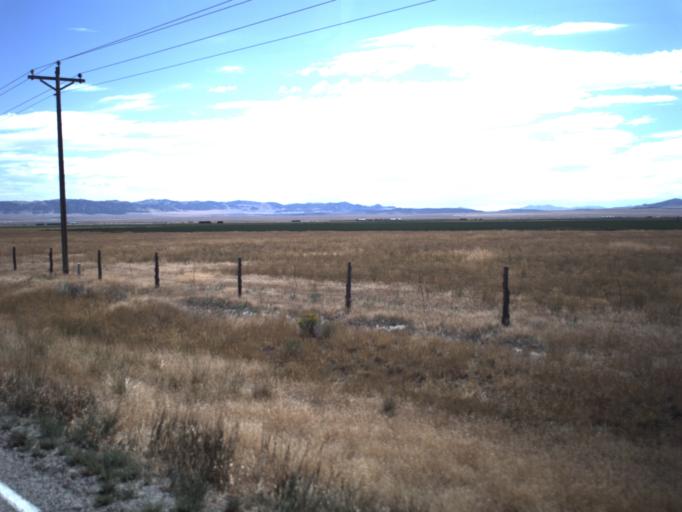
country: US
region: Idaho
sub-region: Oneida County
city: Malad City
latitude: 41.9663
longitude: -112.9401
